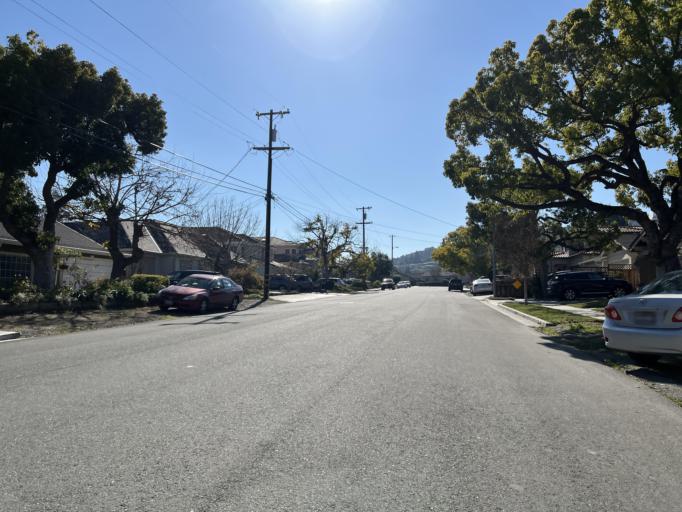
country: US
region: California
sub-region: Santa Clara County
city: Loyola
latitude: 37.3212
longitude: -122.0735
